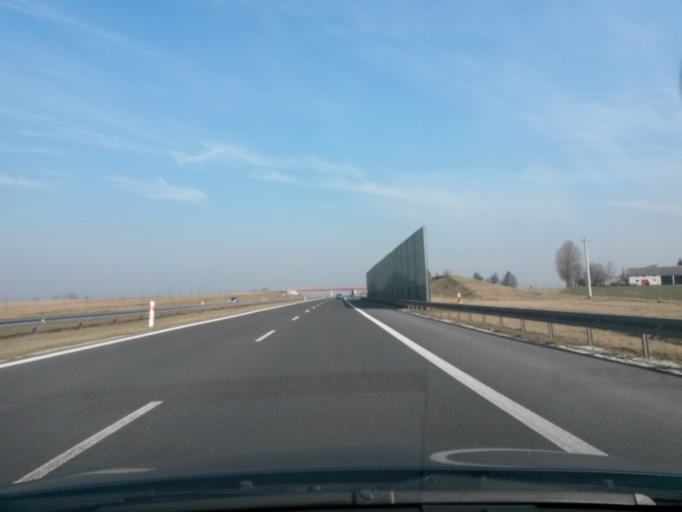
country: PL
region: Lodz Voivodeship
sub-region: Powiat kutnowski
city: Krzyzanow
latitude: 52.1522
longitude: 19.4819
